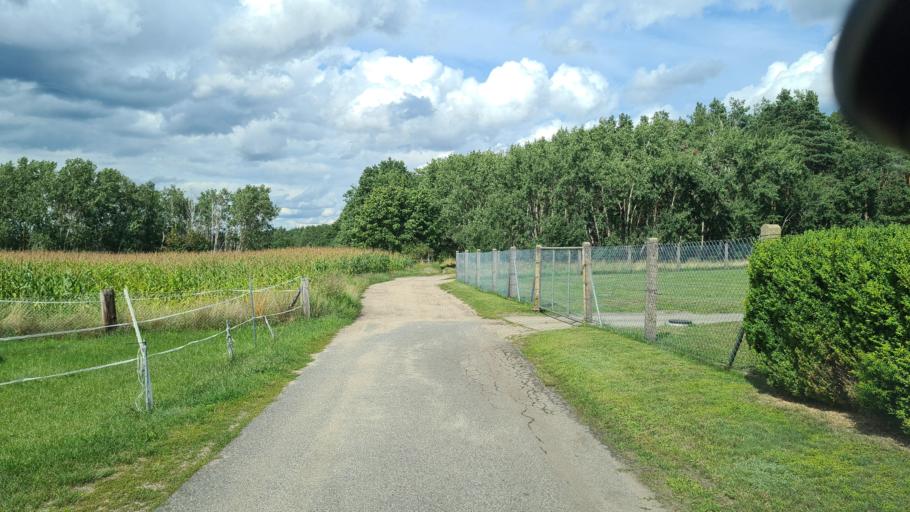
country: DE
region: Brandenburg
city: Drebkau
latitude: 51.6384
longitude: 14.2577
